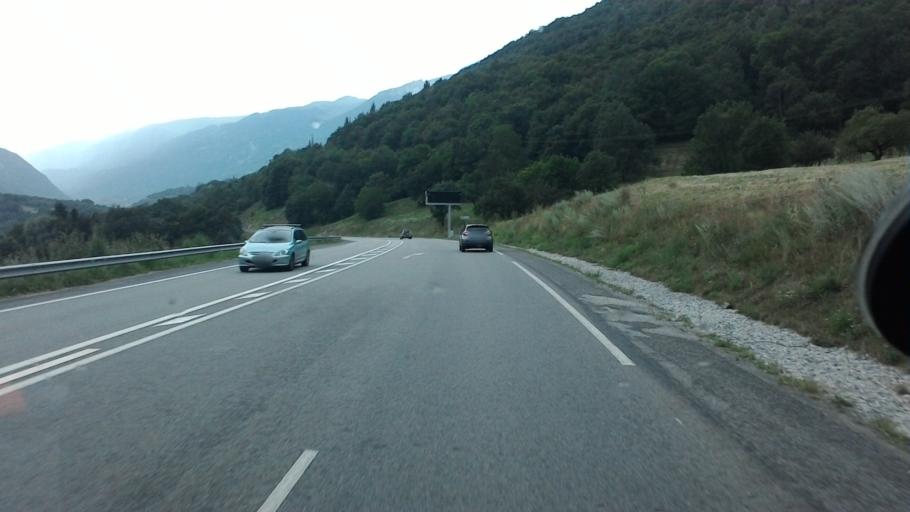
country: FR
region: Rhone-Alpes
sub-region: Departement de la Savoie
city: Macot-la-Plagne
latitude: 45.5682
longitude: 6.7064
